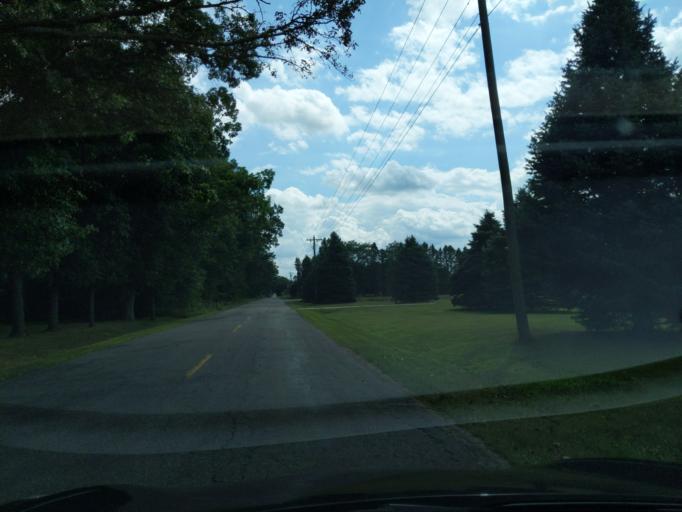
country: US
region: Michigan
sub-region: Eaton County
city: Eaton Rapids
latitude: 42.4917
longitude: -84.5809
